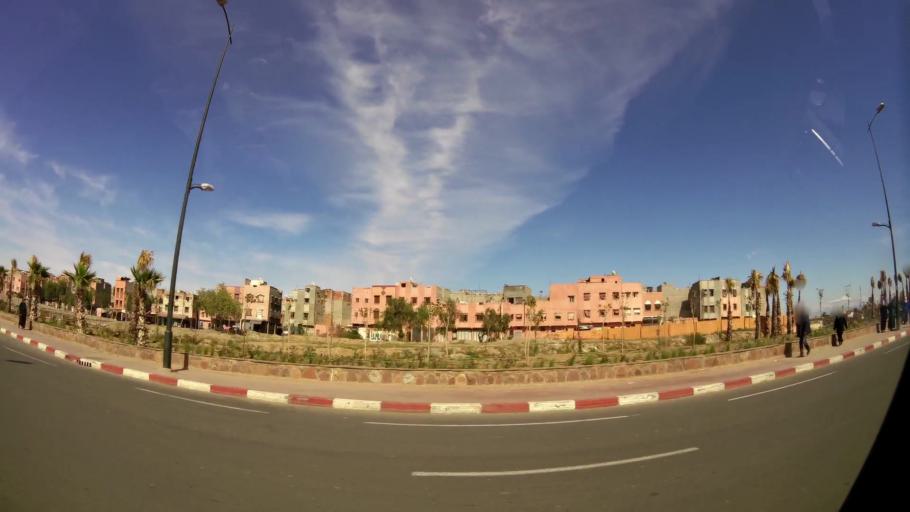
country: MA
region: Marrakech-Tensift-Al Haouz
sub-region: Marrakech
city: Marrakesh
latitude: 31.6349
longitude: -7.9788
